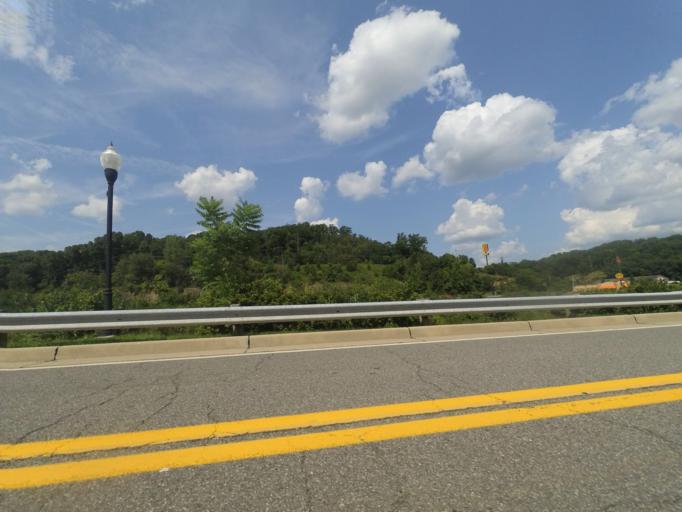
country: US
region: West Virginia
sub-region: Cabell County
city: Huntington
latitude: 38.3951
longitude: -82.4158
